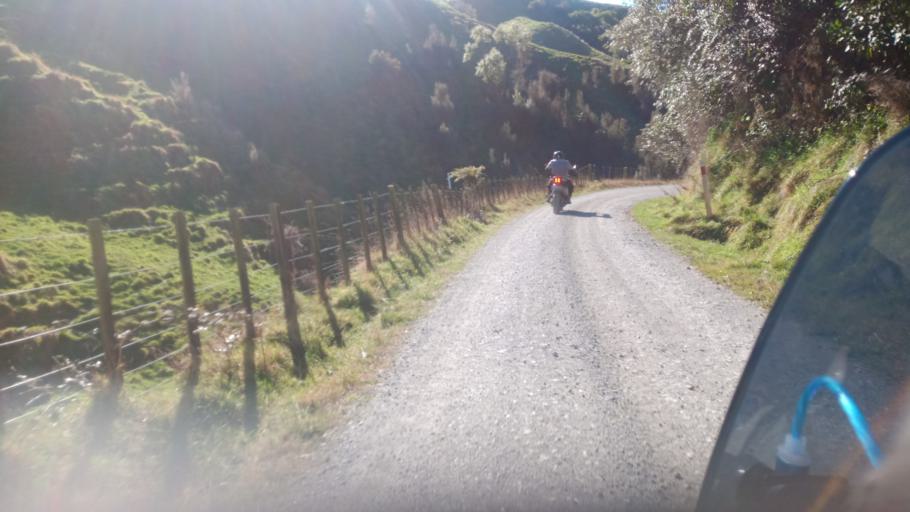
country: NZ
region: Hawke's Bay
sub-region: Wairoa District
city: Wairoa
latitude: -38.6624
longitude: 177.4864
